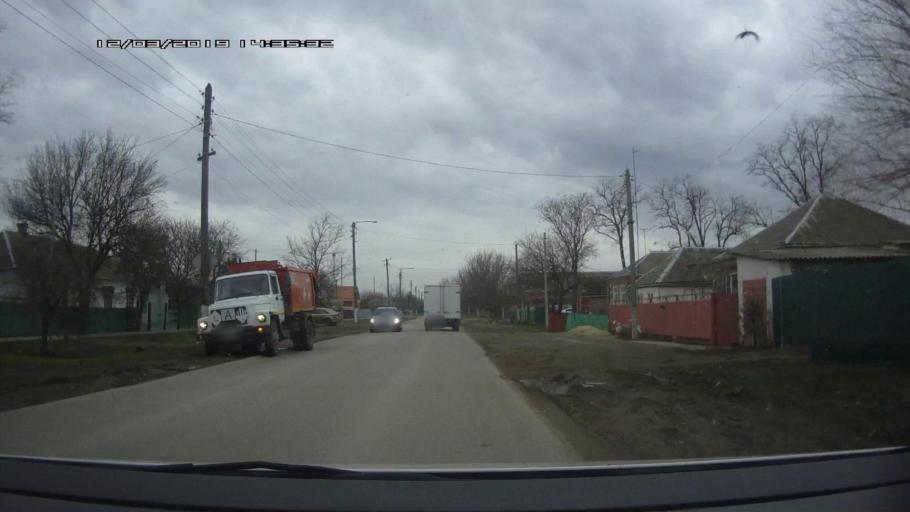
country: RU
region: Rostov
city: Novobataysk
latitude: 46.8972
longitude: 39.7799
